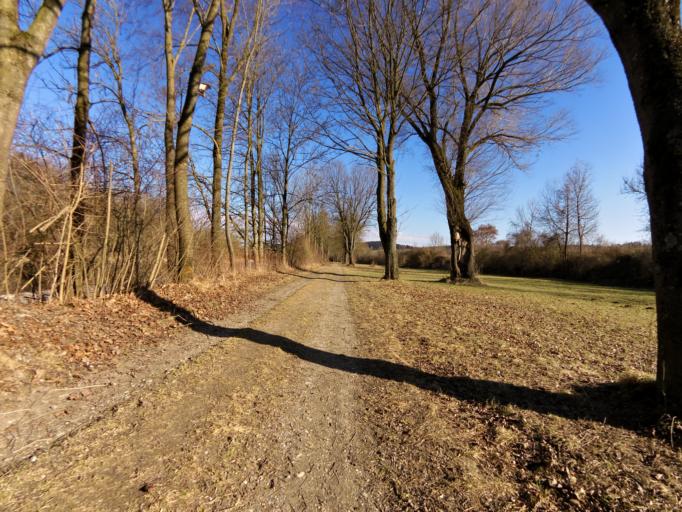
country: DE
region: Bavaria
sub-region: Lower Bavaria
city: Eching
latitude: 48.5064
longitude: 12.0605
